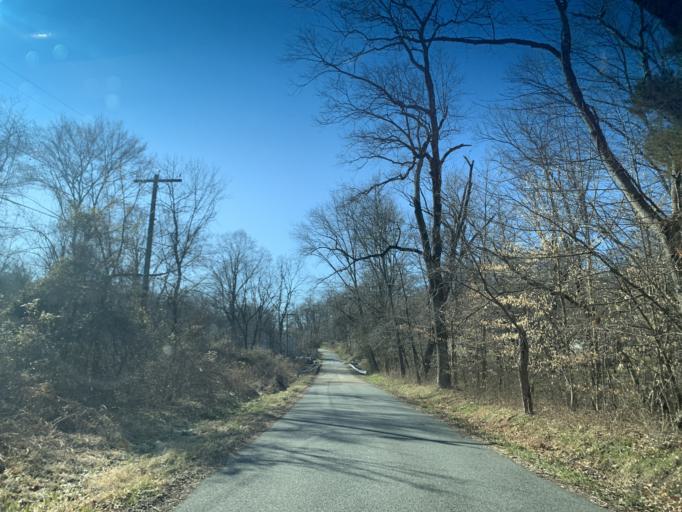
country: US
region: Maryland
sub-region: Cecil County
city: Rising Sun
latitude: 39.6881
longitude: -76.1191
